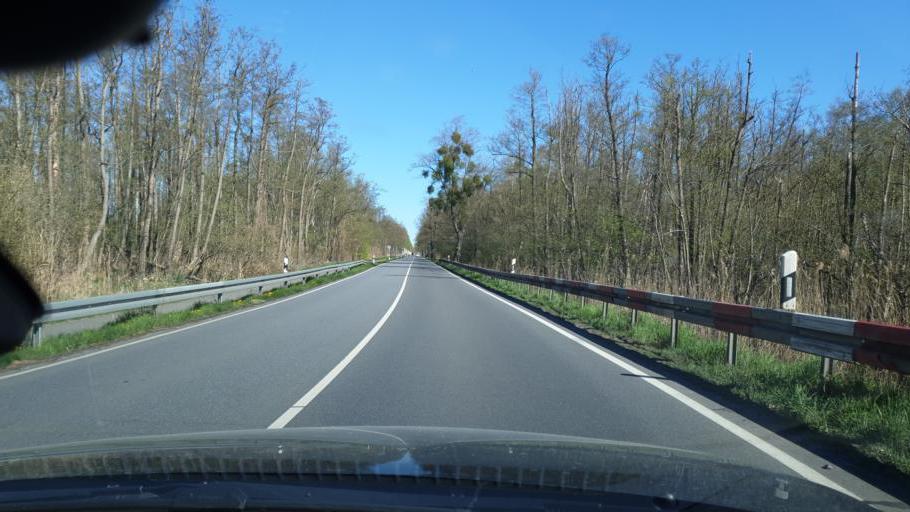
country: DE
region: Mecklenburg-Vorpommern
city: Werdervorstadt
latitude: 53.6622
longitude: 11.4493
